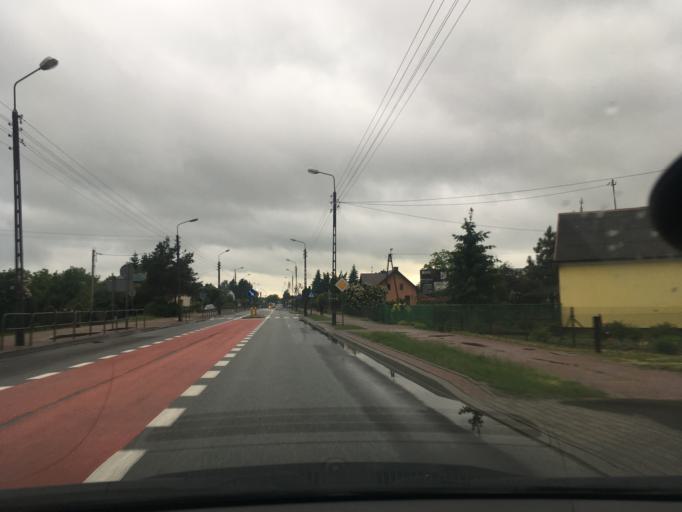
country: PL
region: Lublin Voivodeship
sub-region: Powiat rycki
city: Deblin
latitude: 51.5668
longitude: 21.8786
